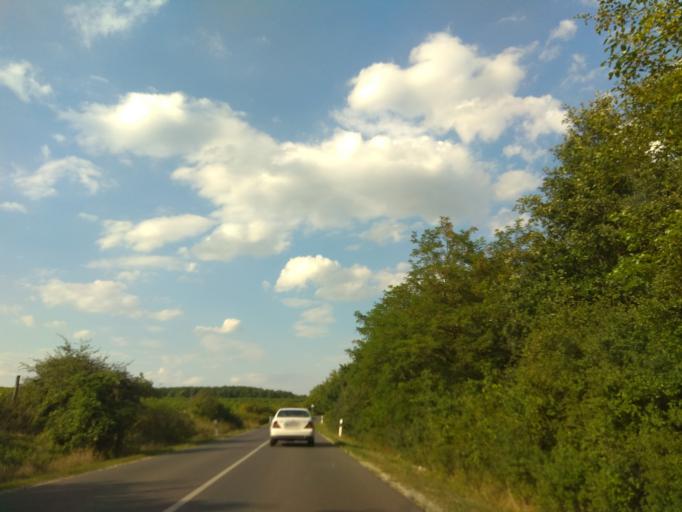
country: HU
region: Borsod-Abauj-Zemplen
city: Harsany
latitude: 47.9851
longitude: 20.7483
